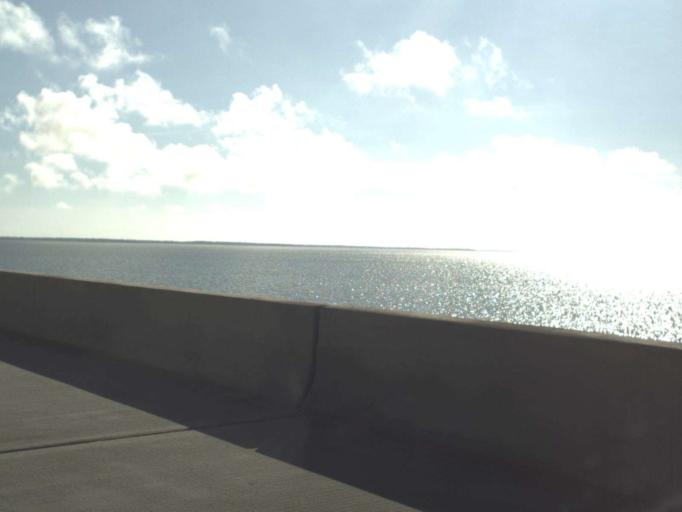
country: US
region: Florida
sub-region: Franklin County
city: Eastpoint
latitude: 29.7000
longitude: -84.8902
